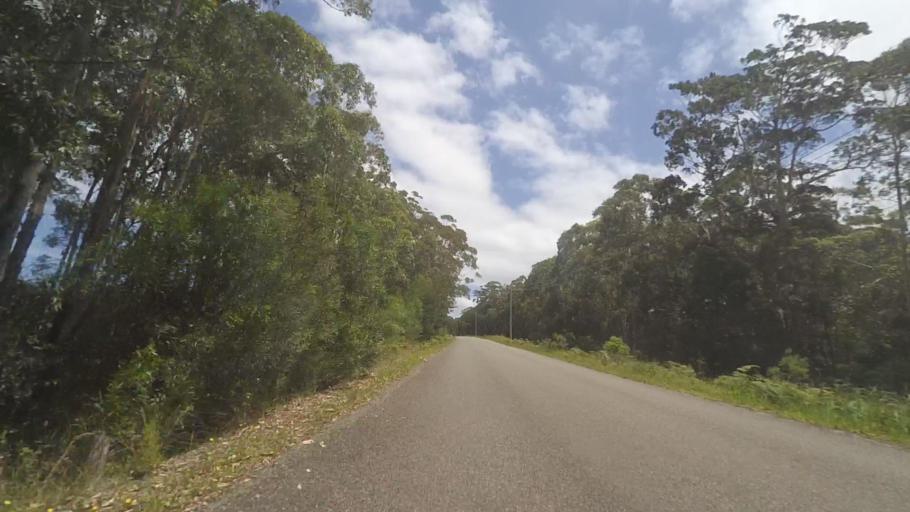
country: AU
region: New South Wales
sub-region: Shoalhaven Shire
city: Milton
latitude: -35.4074
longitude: 150.3579
